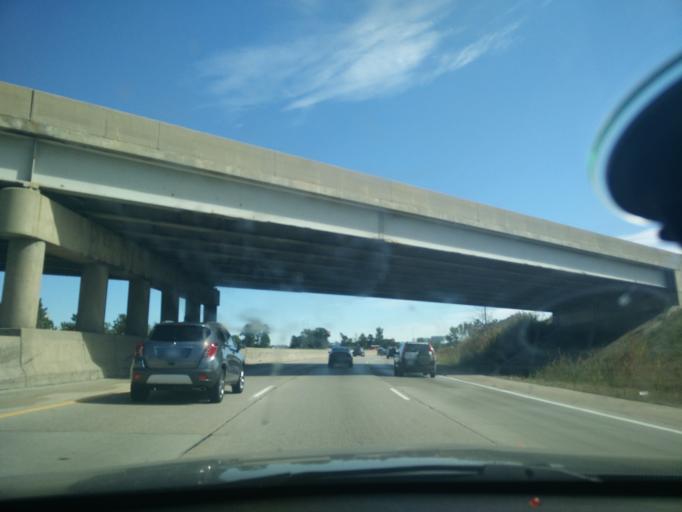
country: US
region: Michigan
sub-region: Oakland County
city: Franklin
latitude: 42.4943
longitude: -83.2959
